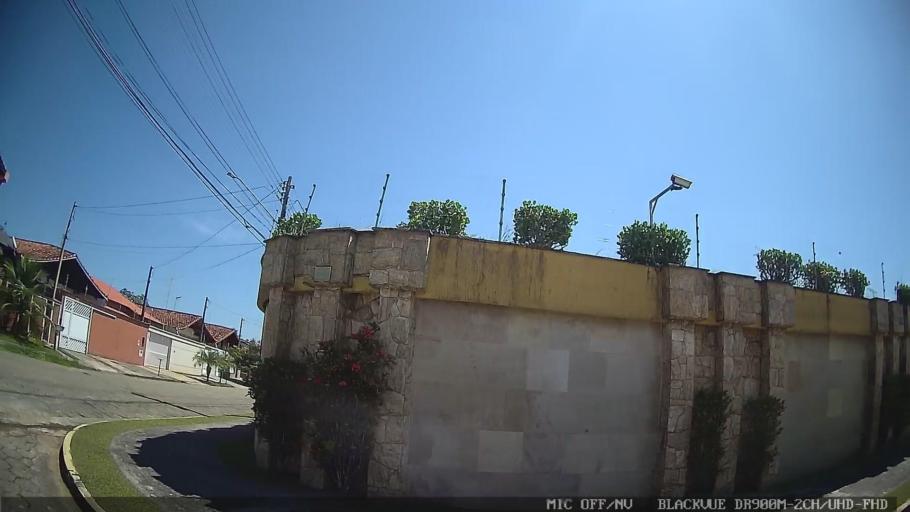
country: BR
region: Sao Paulo
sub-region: Peruibe
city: Peruibe
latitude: -24.2858
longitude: -46.9642
